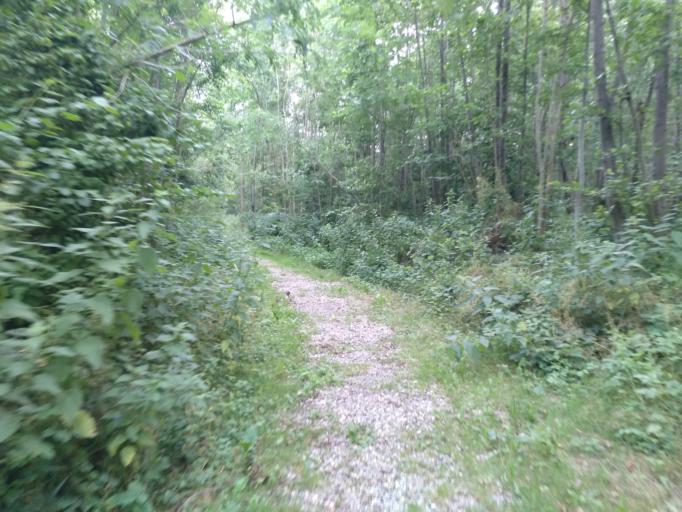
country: FR
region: Rhone-Alpes
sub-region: Departement du Rhone
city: Marennes
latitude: 45.6336
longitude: 4.9243
